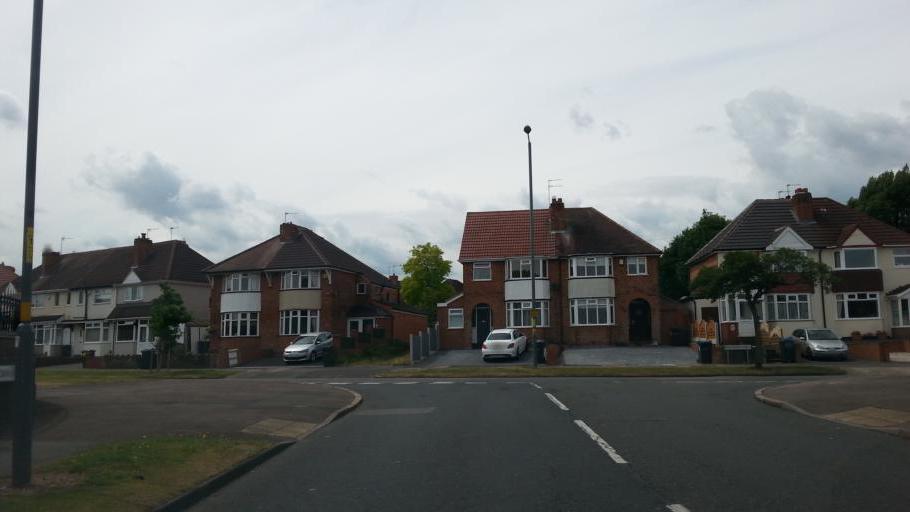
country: GB
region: England
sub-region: City and Borough of Birmingham
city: Acocks Green
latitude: 52.4580
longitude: -1.7902
